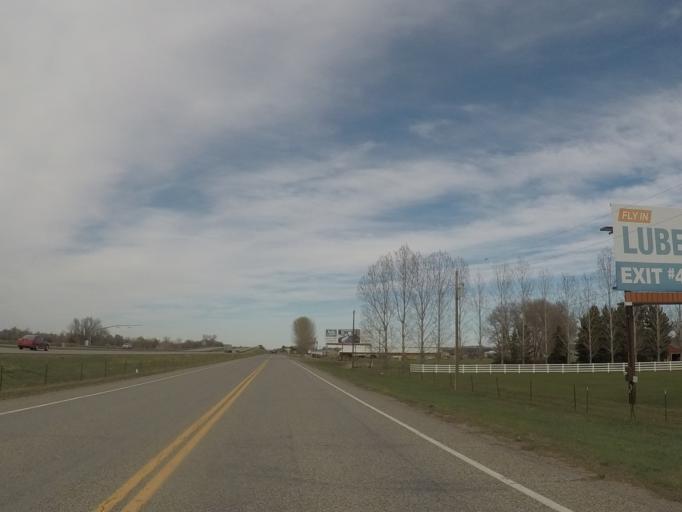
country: US
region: Montana
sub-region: Yellowstone County
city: Laurel
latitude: 45.7017
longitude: -108.6653
